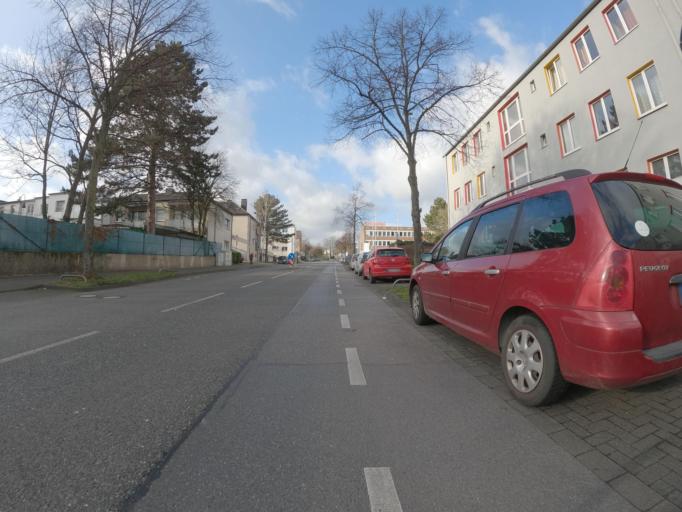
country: DE
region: North Rhine-Westphalia
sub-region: Regierungsbezirk Koln
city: Aachen
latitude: 50.7824
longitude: 6.1012
